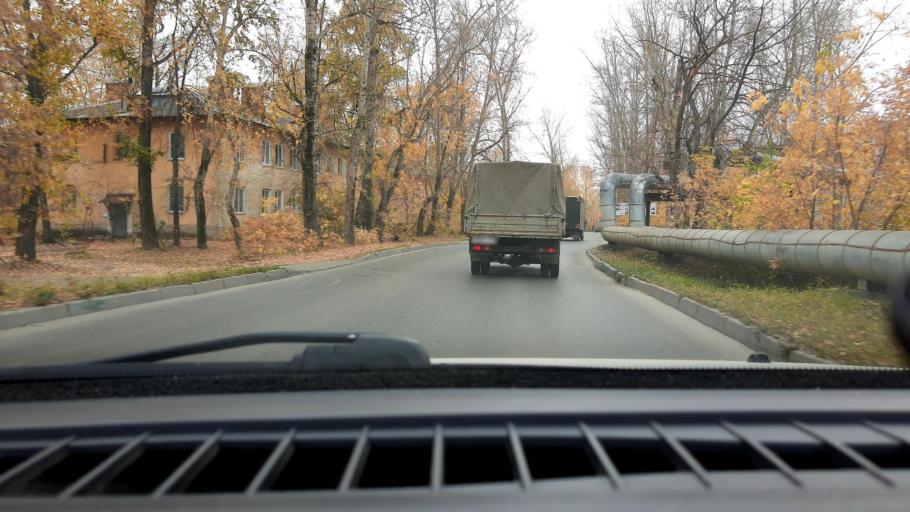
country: RU
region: Nizjnij Novgorod
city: Gorbatovka
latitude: 56.3429
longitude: 43.8237
